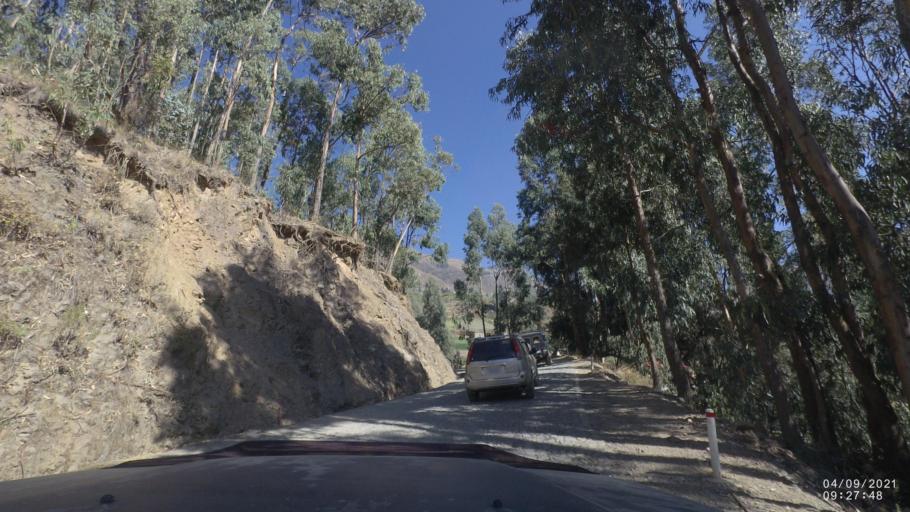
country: BO
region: Cochabamba
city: Sipe Sipe
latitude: -17.3572
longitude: -66.3729
